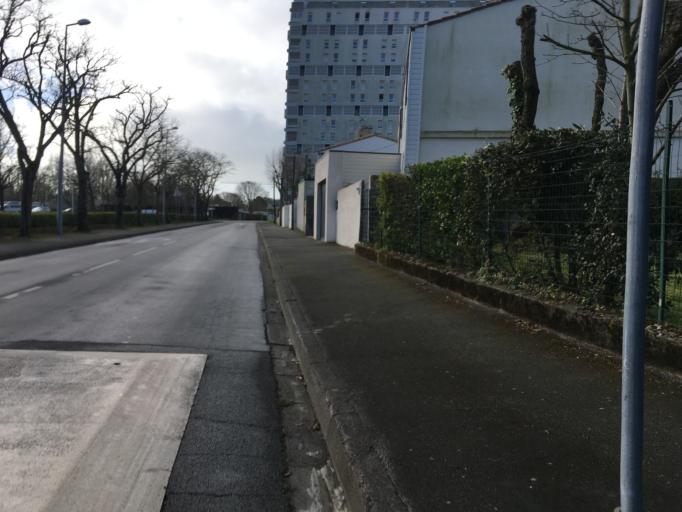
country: FR
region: Poitou-Charentes
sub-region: Departement de la Charente-Maritime
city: La Rochelle
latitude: 46.1693
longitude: -1.1870
